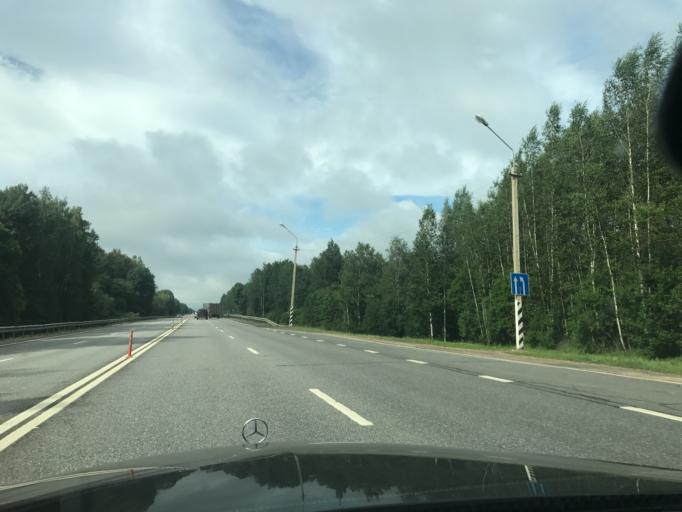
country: RU
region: Smolensk
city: Kardymovo
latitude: 55.0082
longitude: 32.2862
